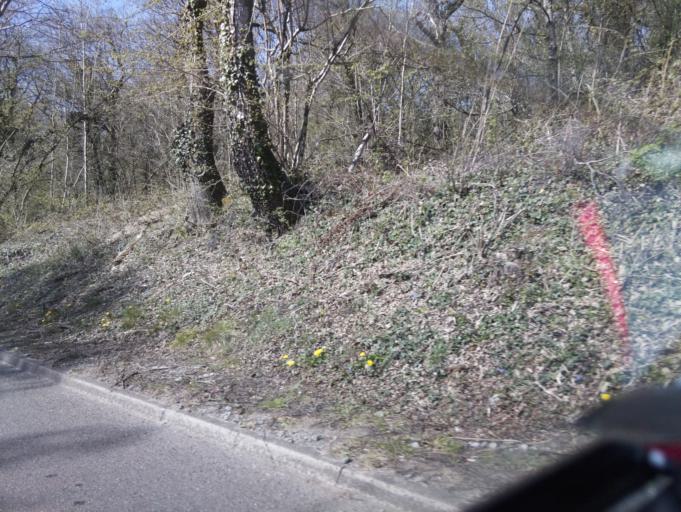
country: GB
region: Wales
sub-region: Rhondda Cynon Taf
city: Mountain Ash
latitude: 51.6646
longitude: -3.3481
